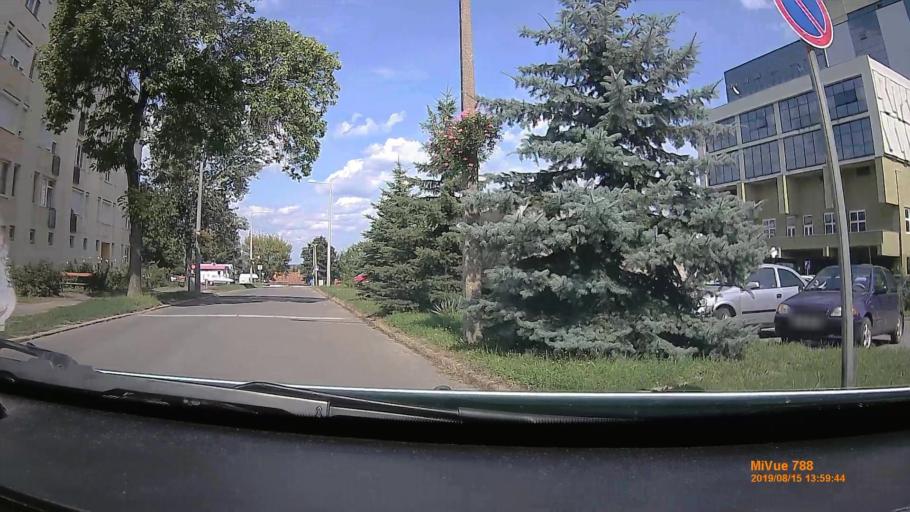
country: HU
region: Borsod-Abauj-Zemplen
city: Kazincbarcika
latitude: 48.2549
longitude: 20.6178
